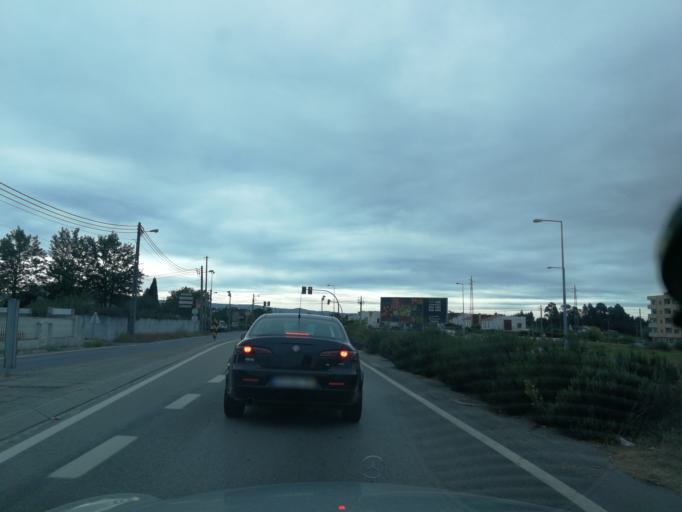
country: PT
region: Aveiro
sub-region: Agueda
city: Agueda
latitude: 40.5915
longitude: -8.4539
